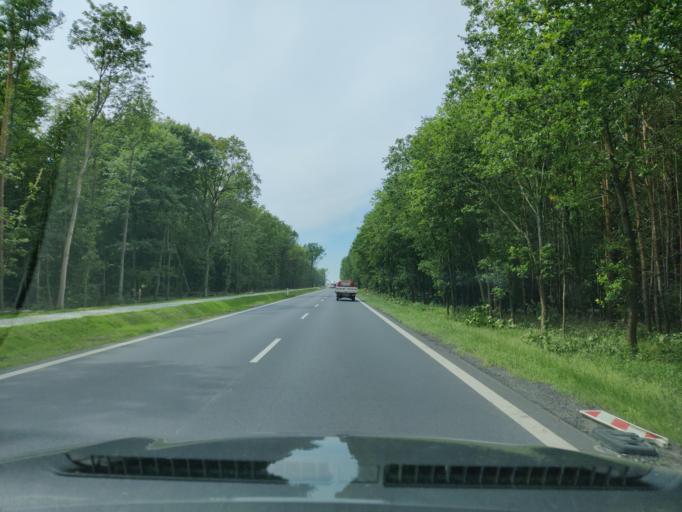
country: PL
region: Greater Poland Voivodeship
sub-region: Powiat grodziski
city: Granowo
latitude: 52.2312
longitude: 16.5952
